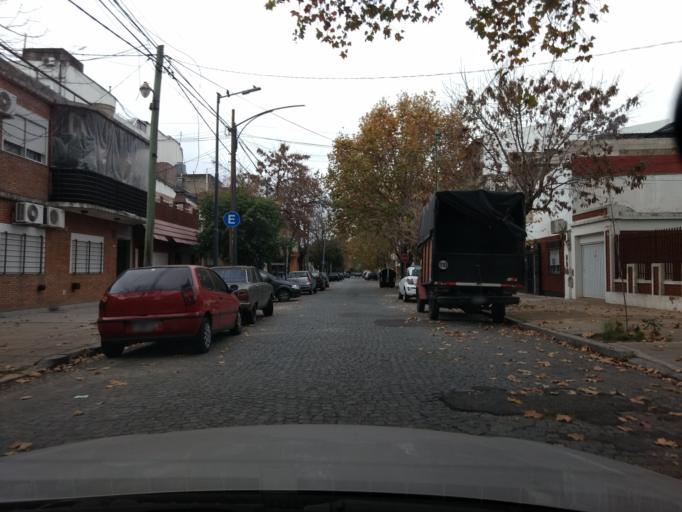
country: AR
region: Buenos Aires F.D.
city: Villa Santa Rita
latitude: -34.6231
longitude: -58.5173
